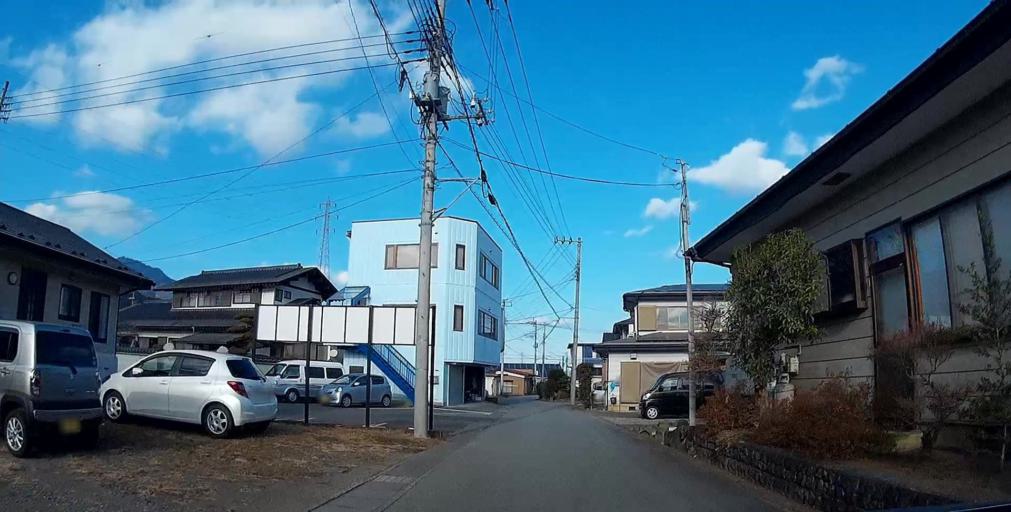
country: JP
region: Yamanashi
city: Fujikawaguchiko
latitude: 35.4946
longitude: 138.8194
